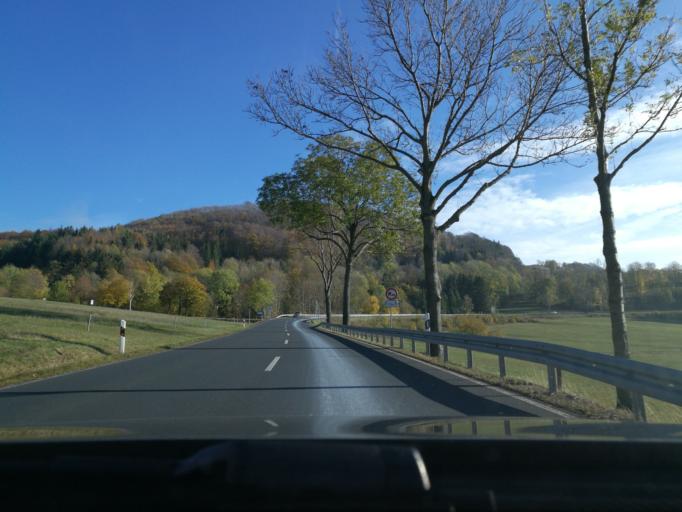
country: DE
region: Hesse
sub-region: Regierungsbezirk Kassel
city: Gersfeld
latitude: 50.4326
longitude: 9.9259
